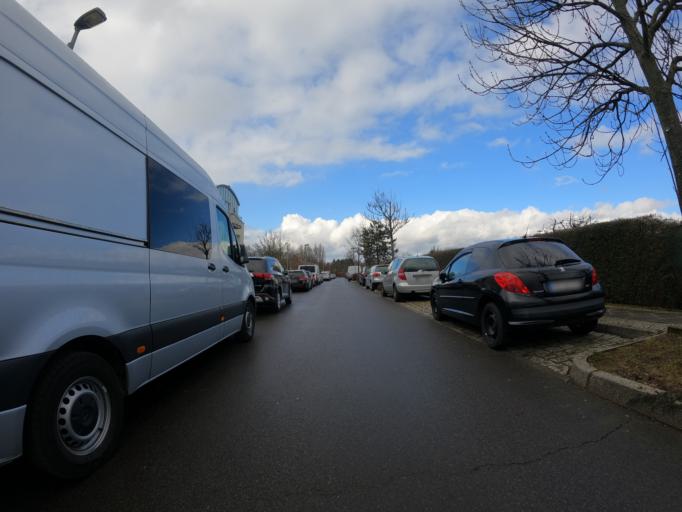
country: DE
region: Berlin
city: Kaulsdorf
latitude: 52.5294
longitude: 13.5770
